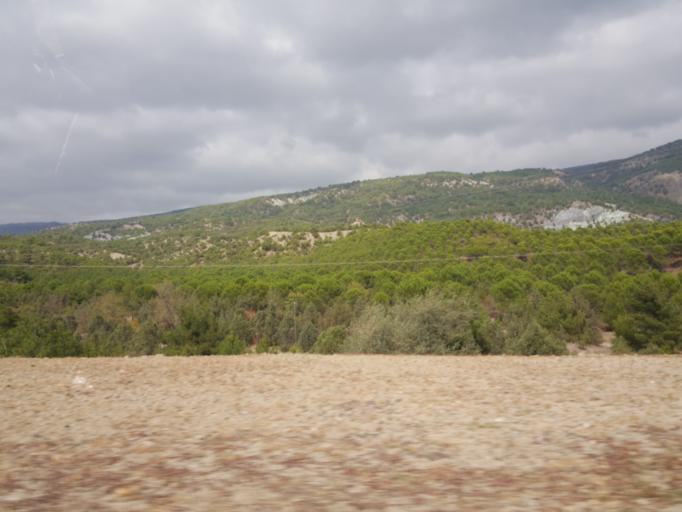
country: TR
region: Corum
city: Hacihamza
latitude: 41.0989
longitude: 34.3606
